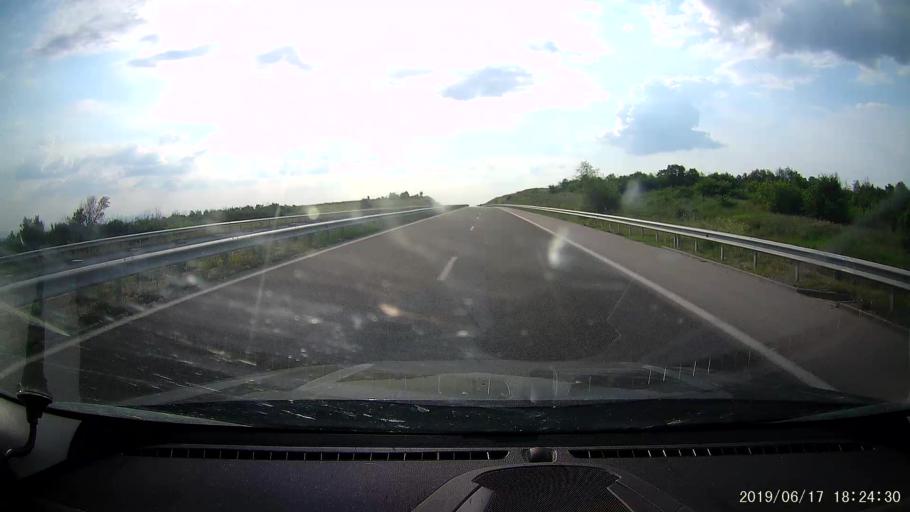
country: BG
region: Khaskovo
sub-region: Obshtina Dimitrovgrad
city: Dimitrovgrad
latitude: 41.9853
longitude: 25.6896
